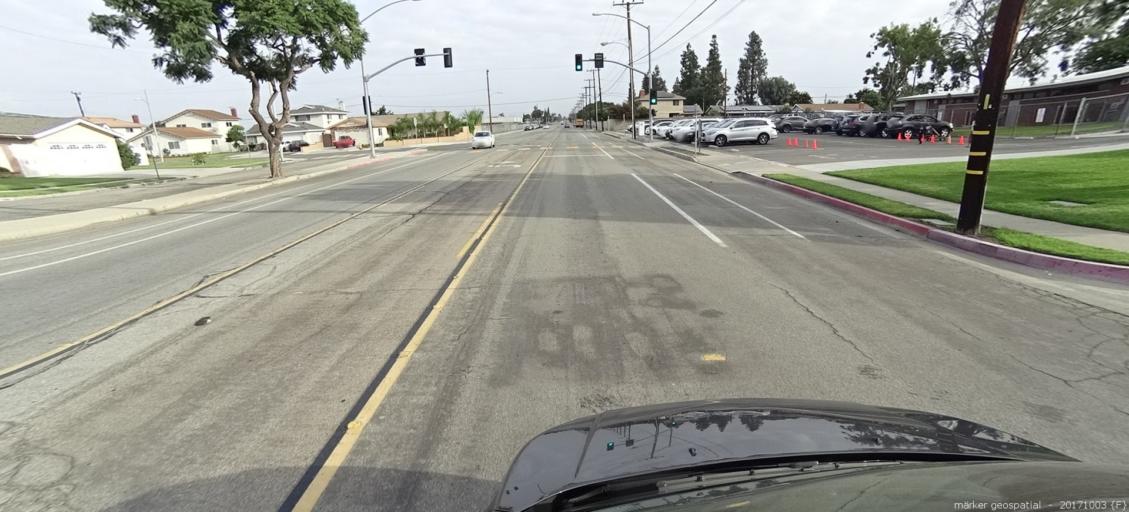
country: US
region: California
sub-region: Orange County
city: Fountain Valley
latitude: 33.7333
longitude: -117.9460
